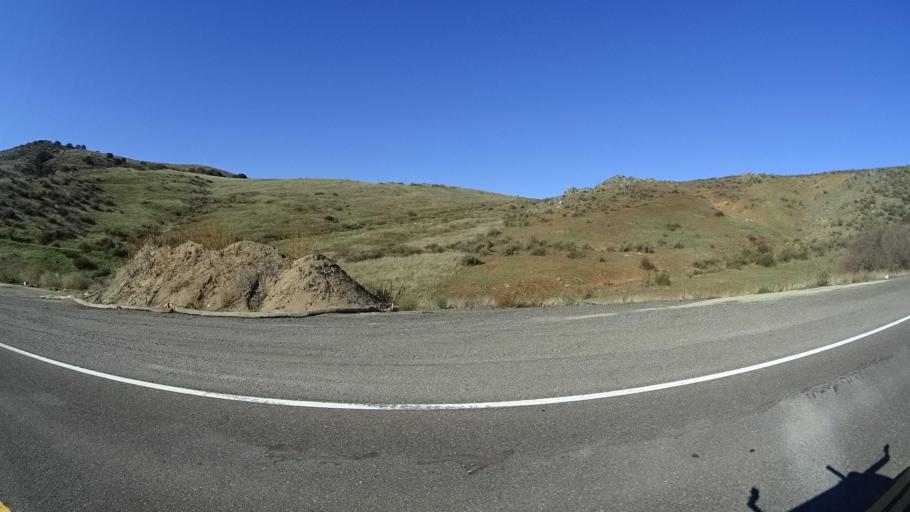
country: US
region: California
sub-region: San Diego County
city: Jamul
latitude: 32.6792
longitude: -116.8400
